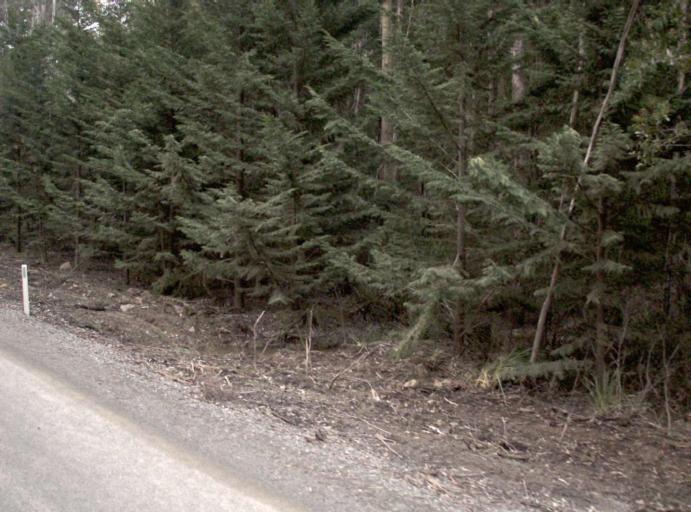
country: AU
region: Tasmania
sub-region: Launceston
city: Newstead
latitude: -41.3670
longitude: 147.2349
